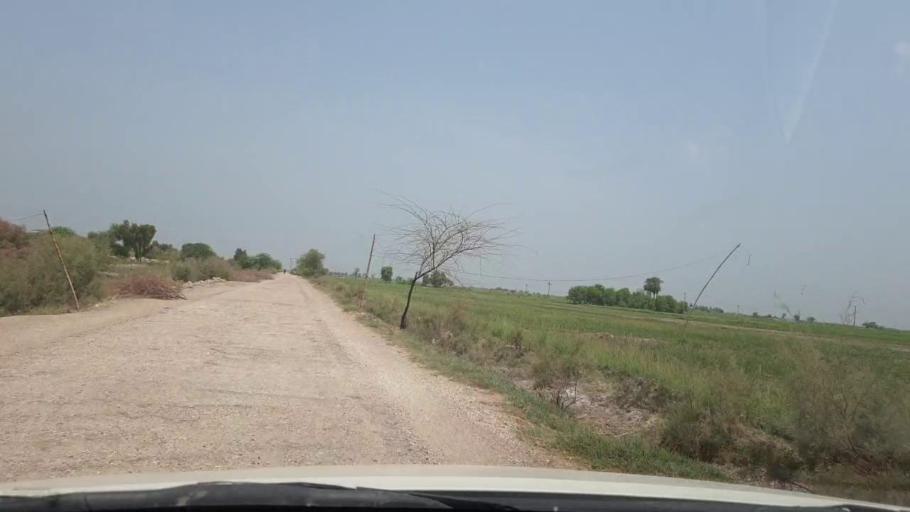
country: PK
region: Sindh
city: Rustam jo Goth
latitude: 28.0444
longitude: 68.8150
